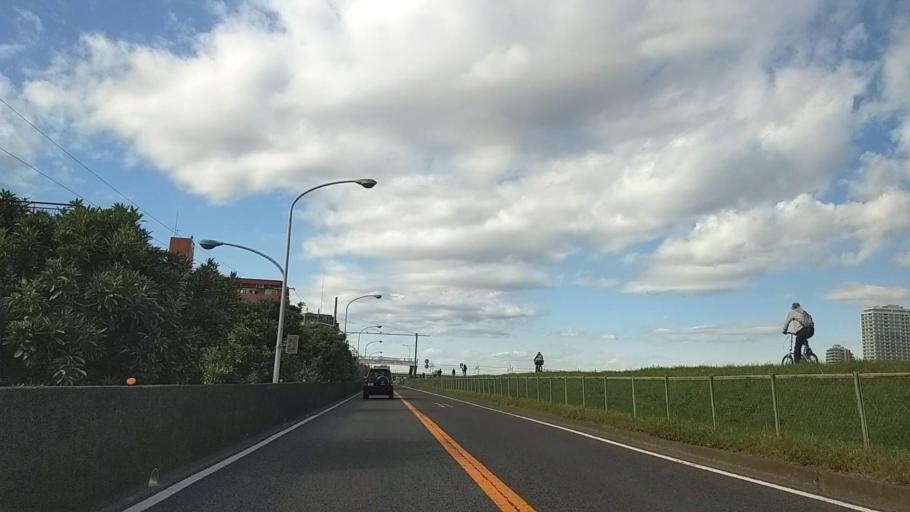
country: JP
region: Tokyo
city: Chofugaoka
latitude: 35.6049
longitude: 139.6285
